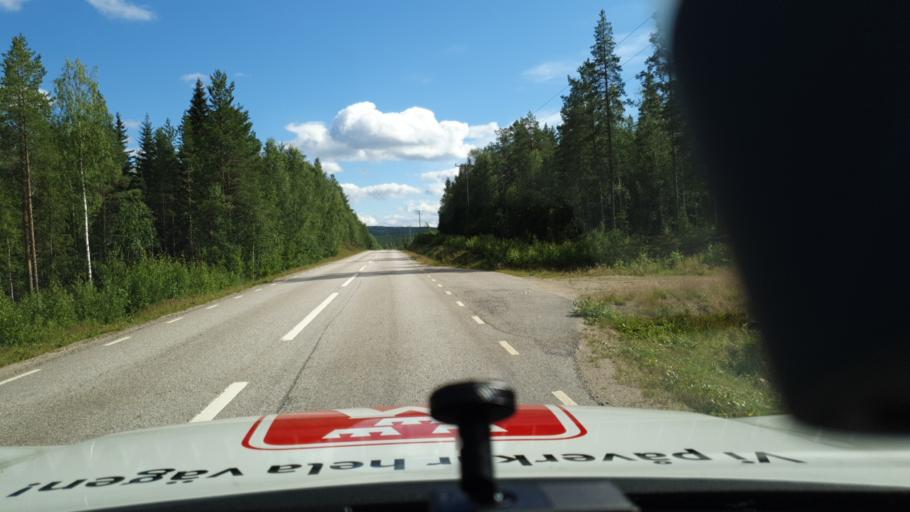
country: NO
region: Hedmark
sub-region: Trysil
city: Innbygda
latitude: 61.0022
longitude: 12.4860
